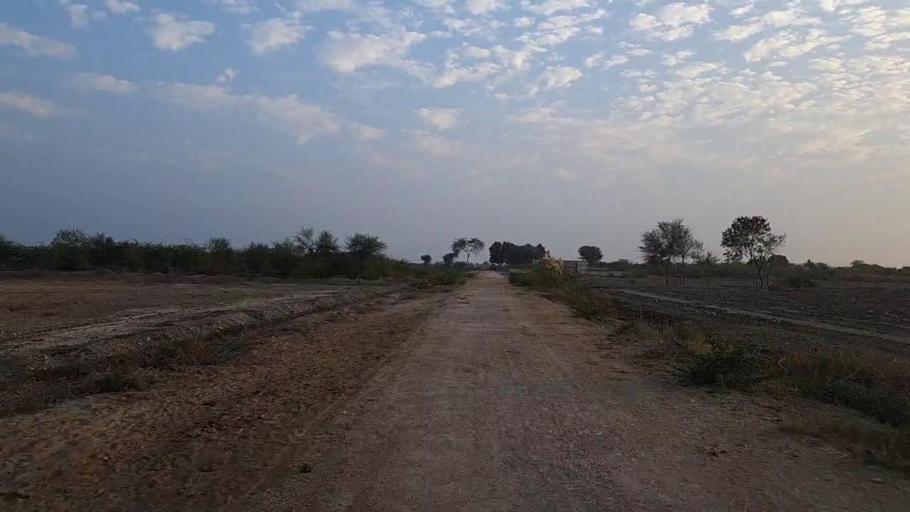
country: PK
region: Sindh
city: Pithoro
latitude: 25.4424
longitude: 69.3380
